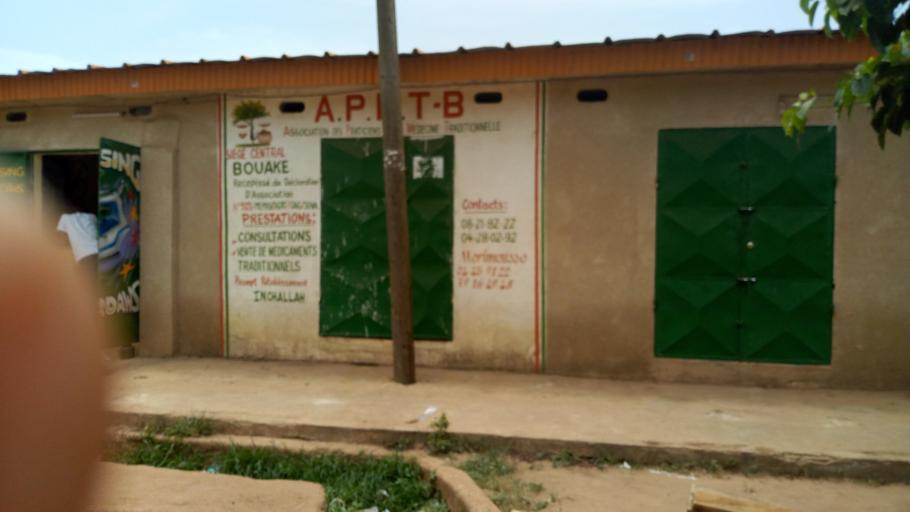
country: CI
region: Vallee du Bandama
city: Bouake
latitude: 7.7040
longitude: -5.0397
